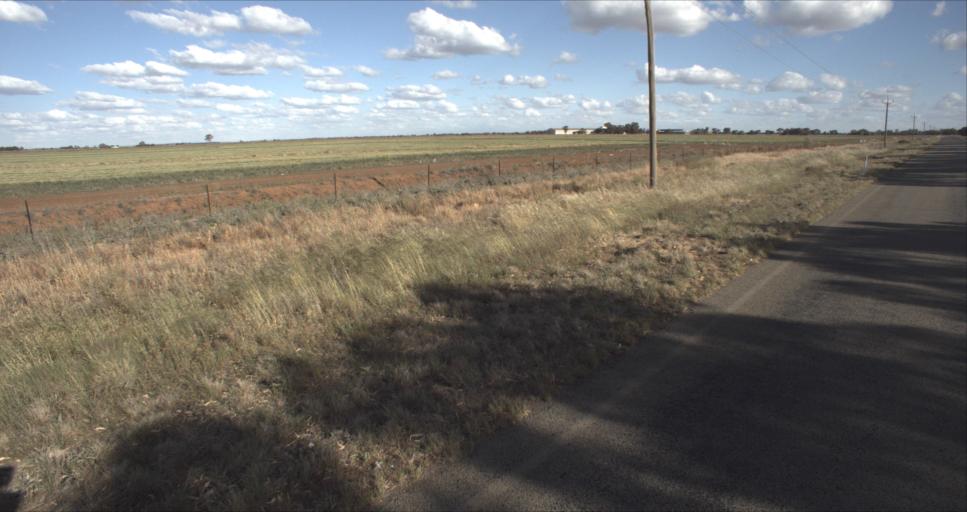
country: AU
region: New South Wales
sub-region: Leeton
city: Leeton
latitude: -34.5437
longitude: 146.2797
